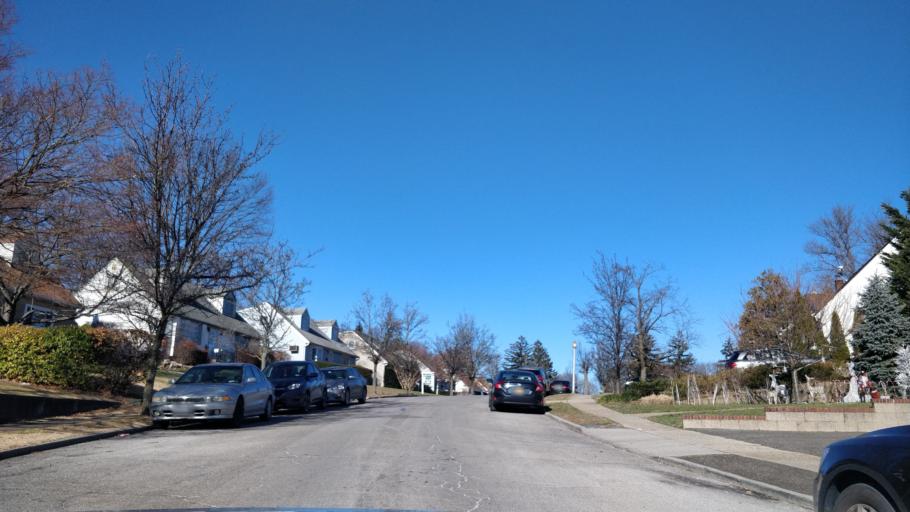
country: US
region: New York
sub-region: Nassau County
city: Glen Cove
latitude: 40.8734
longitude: -73.6245
